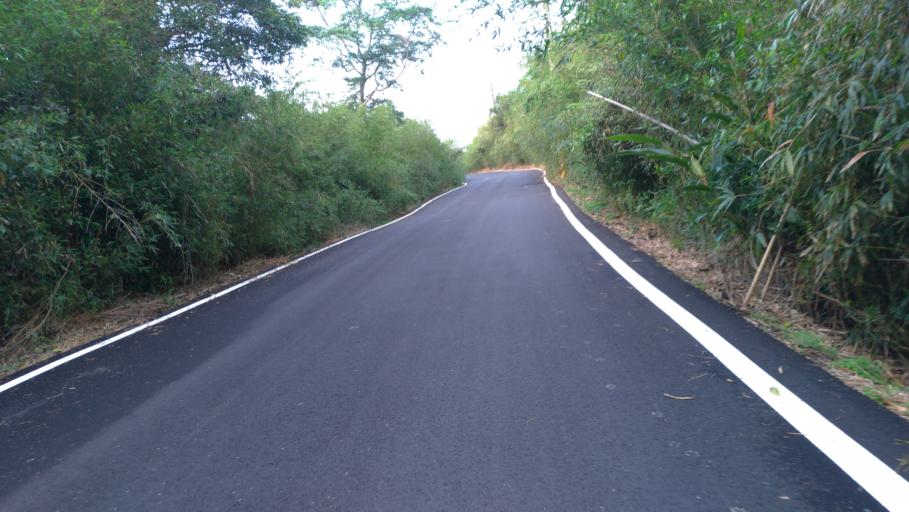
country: TW
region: Taiwan
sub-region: Hsinchu
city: Hsinchu
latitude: 24.7509
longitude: 120.9883
